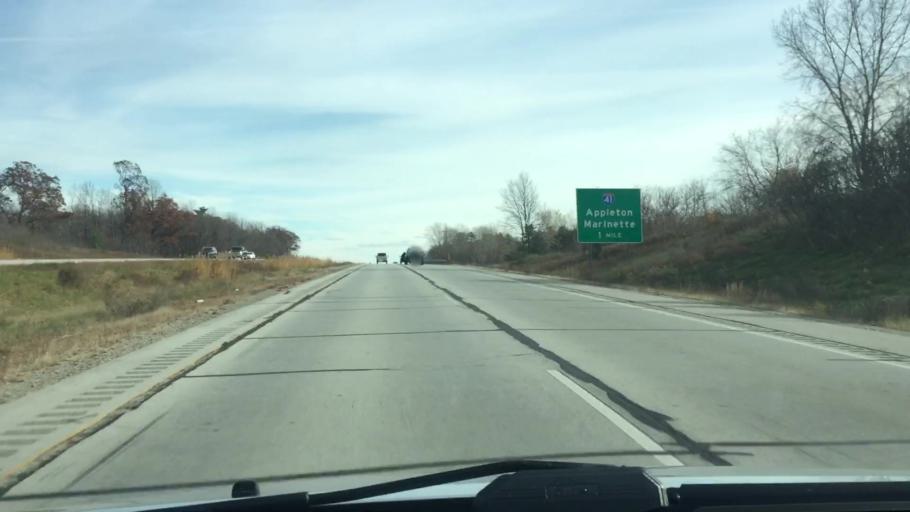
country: US
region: Wisconsin
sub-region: Brown County
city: Howard
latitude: 44.5520
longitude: -88.1102
